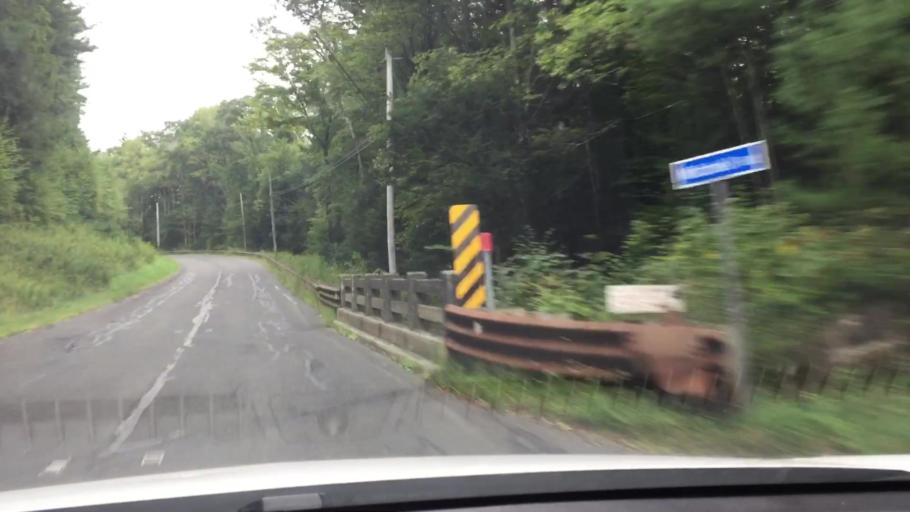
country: US
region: Massachusetts
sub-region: Berkshire County
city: Becket
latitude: 42.2631
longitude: -73.0014
